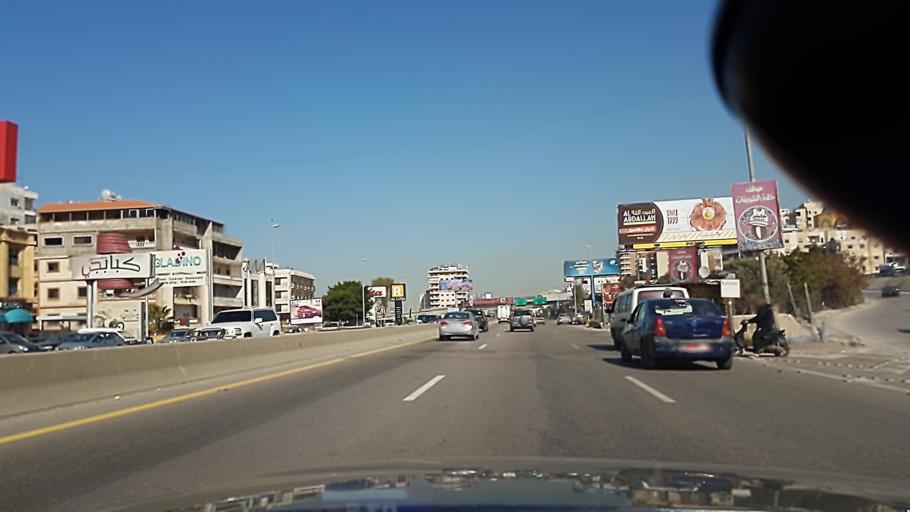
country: LB
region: Mont-Liban
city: Baabda
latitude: 33.7871
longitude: 35.4790
